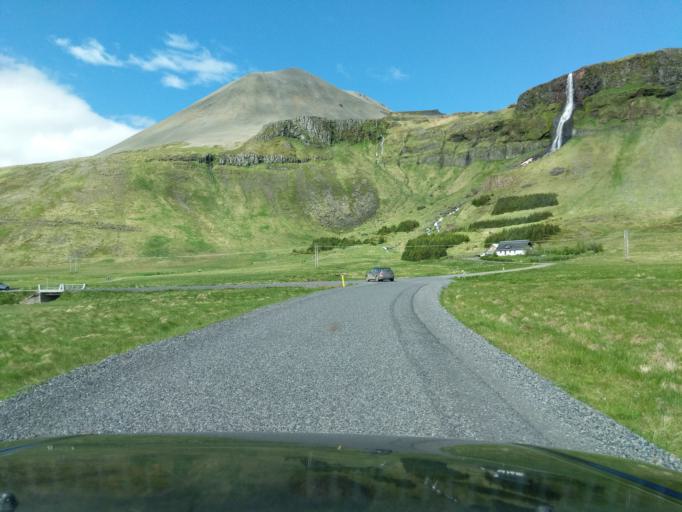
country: IS
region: West
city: Olafsvik
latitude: 64.8423
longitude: -23.3998
